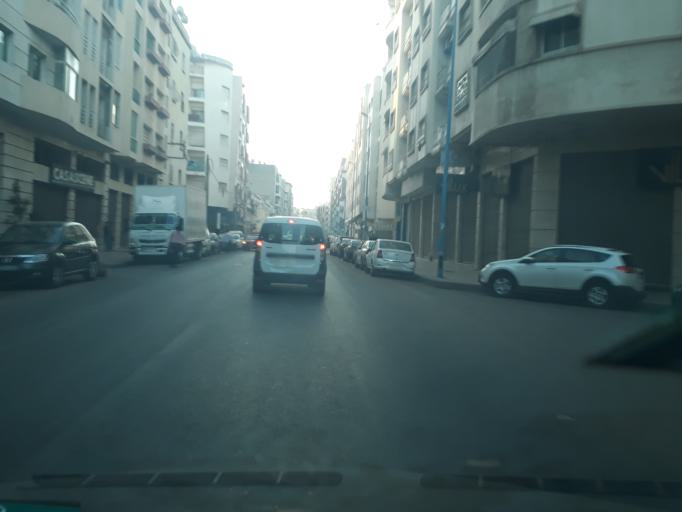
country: MA
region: Grand Casablanca
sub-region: Casablanca
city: Casablanca
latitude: 33.5773
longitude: -7.6446
